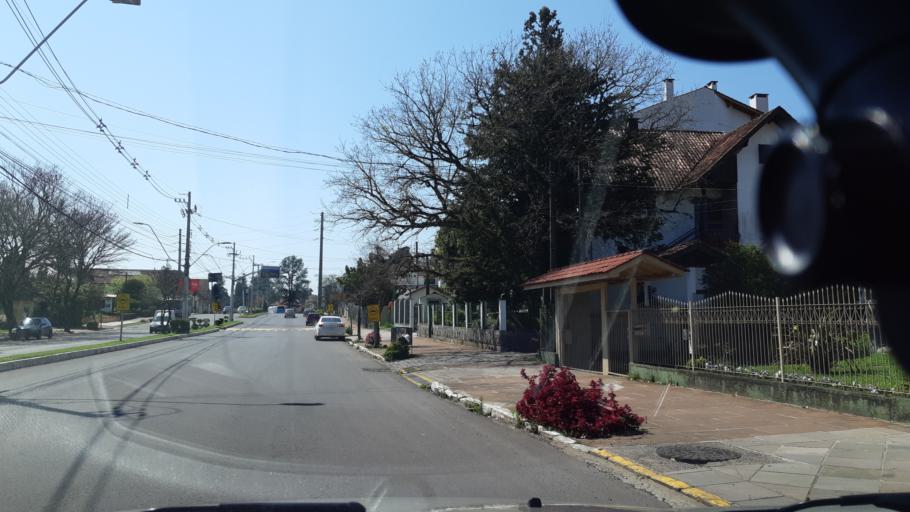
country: BR
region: Rio Grande do Sul
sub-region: Nova Petropolis
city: Nova Petropolis
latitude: -29.3833
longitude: -51.1183
